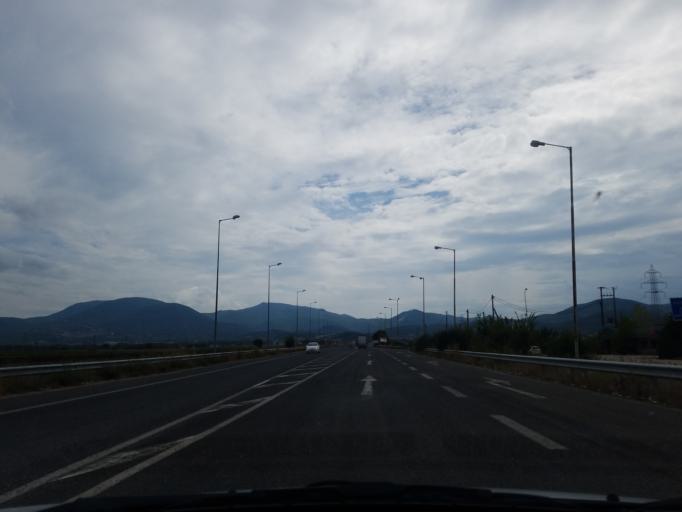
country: GR
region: Central Greece
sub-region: Nomos Fthiotidos
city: Domokos
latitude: 39.0433
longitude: 22.3514
